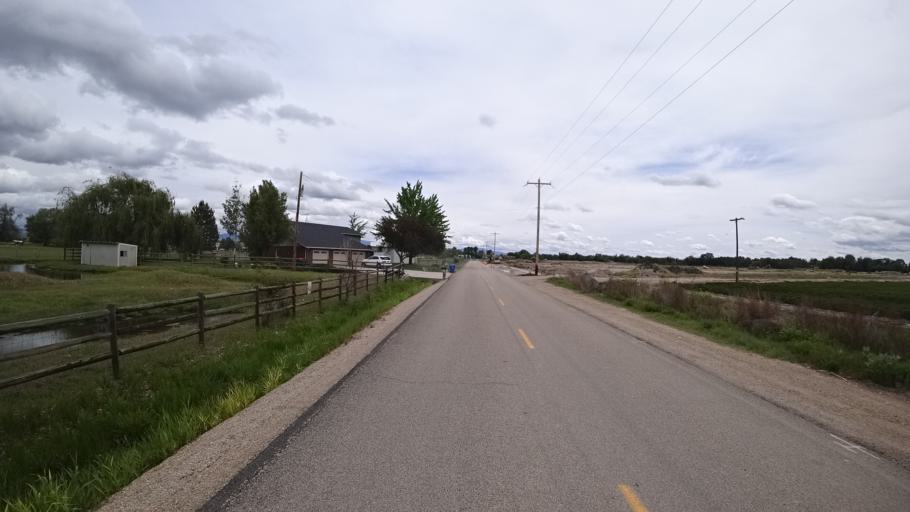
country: US
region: Idaho
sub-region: Ada County
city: Star
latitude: 43.6897
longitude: -116.4548
